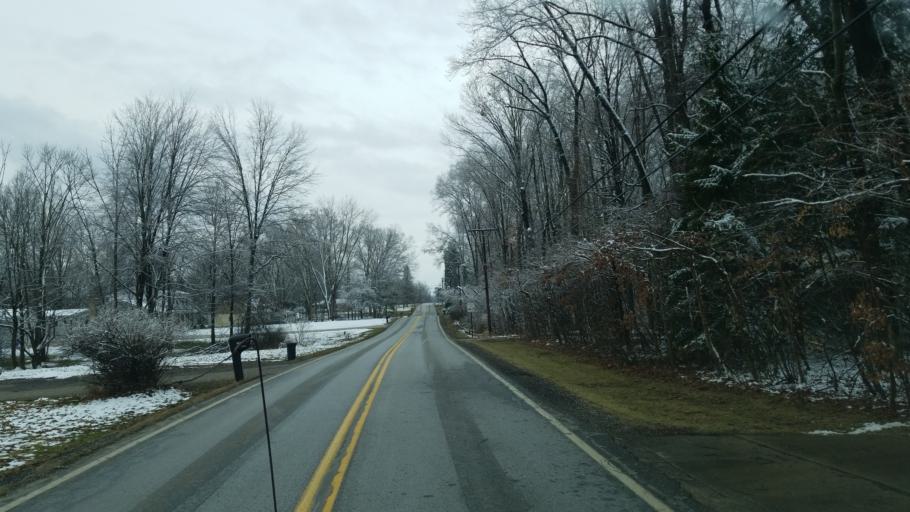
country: US
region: Ohio
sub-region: Portage County
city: Ravenna
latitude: 41.1713
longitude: -81.2131
